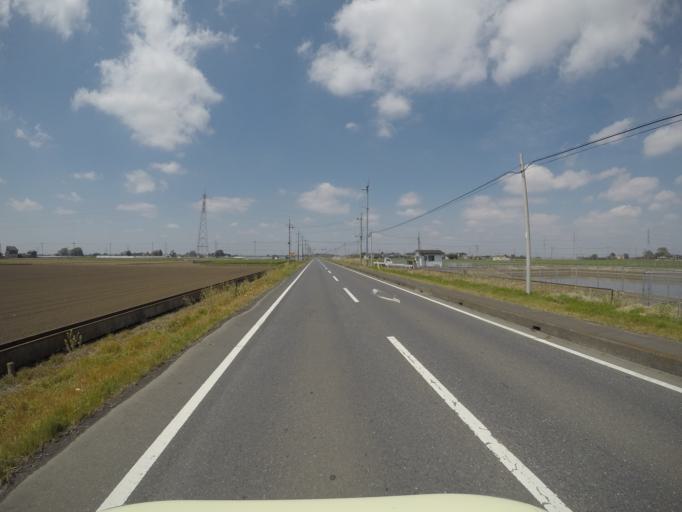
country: JP
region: Ibaraki
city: Shimodate
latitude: 36.3378
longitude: 139.9654
